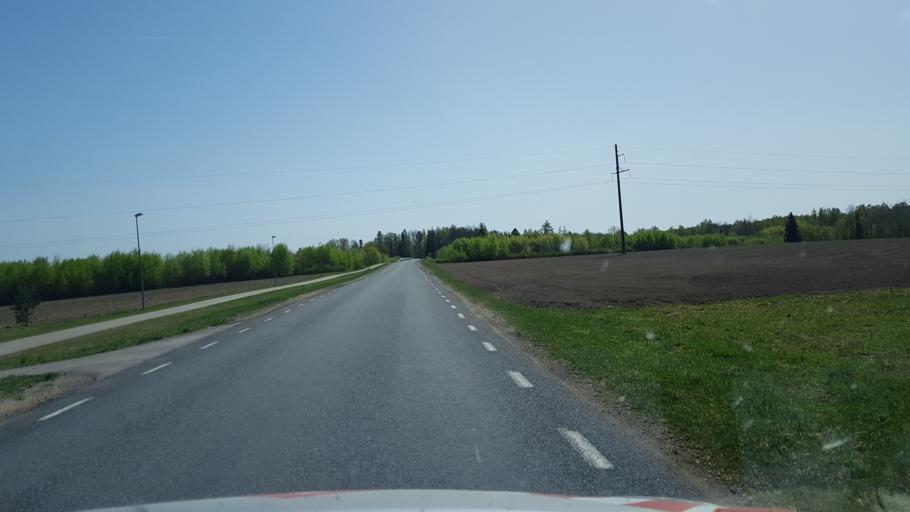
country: EE
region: Viljandimaa
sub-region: Vohma linn
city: Vohma
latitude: 58.5643
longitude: 25.5477
